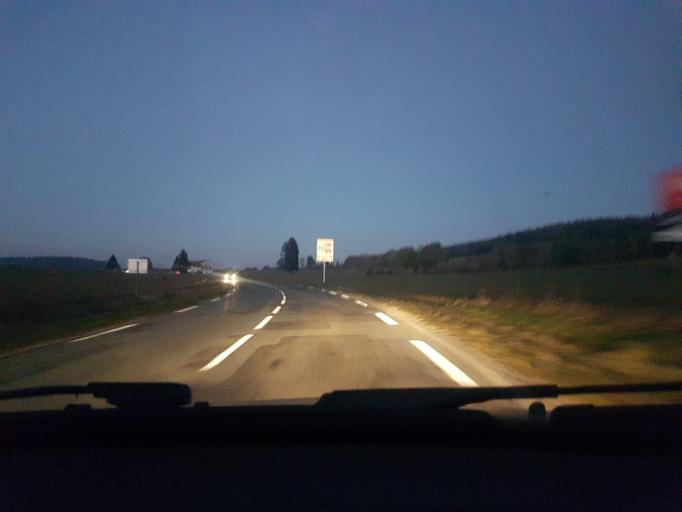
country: FR
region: Franche-Comte
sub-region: Departement du Doubs
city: Les Fins
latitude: 47.0882
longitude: 6.6433
